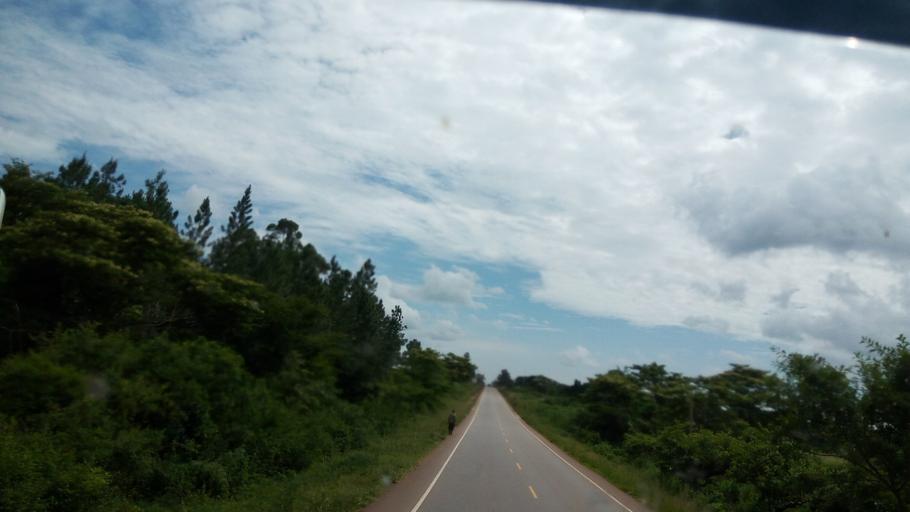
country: UG
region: Central Region
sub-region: Nakasongola District
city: Nakasongola
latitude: 1.1505
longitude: 32.4648
